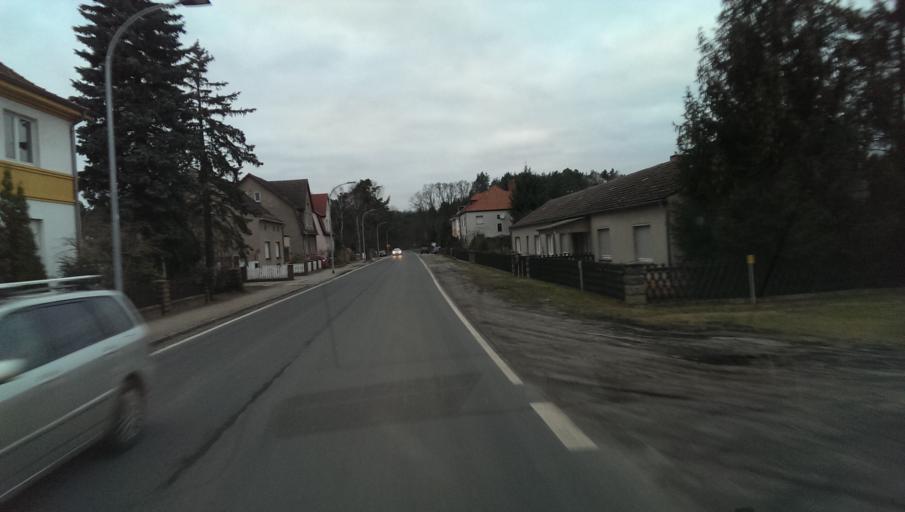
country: DE
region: Brandenburg
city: Sperenberg
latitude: 52.1451
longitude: 13.3611
